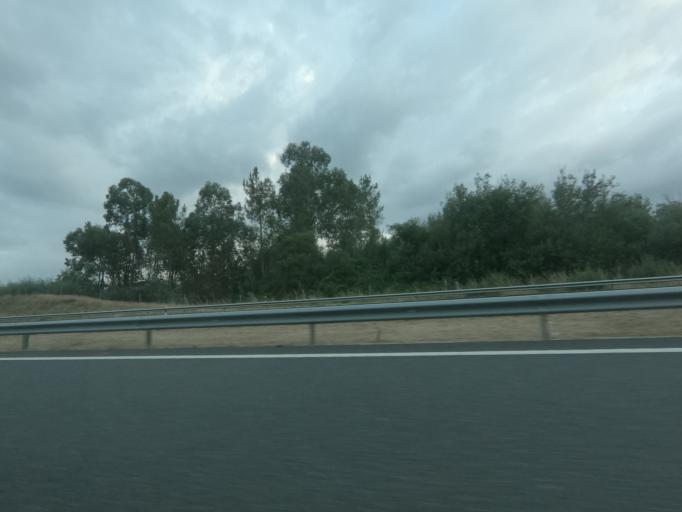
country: ES
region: Galicia
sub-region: Provincia de Ourense
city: Castrelo de Mino
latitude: 42.3335
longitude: -8.0436
